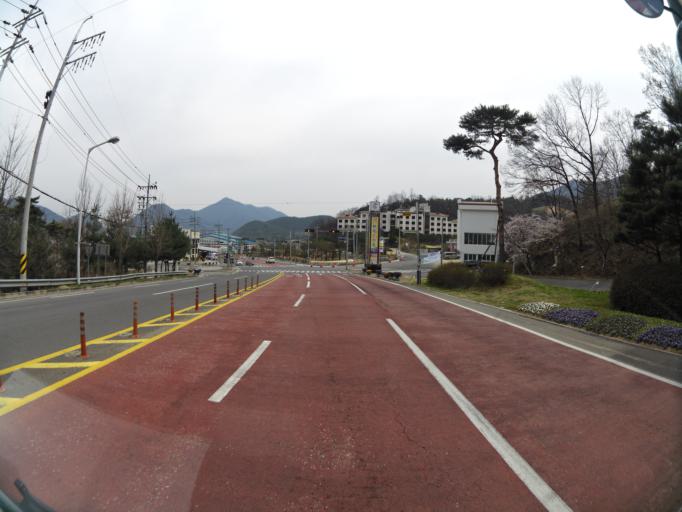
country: KR
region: Gyeongsangnam-do
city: Changnyeong
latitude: 35.4356
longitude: 128.5903
